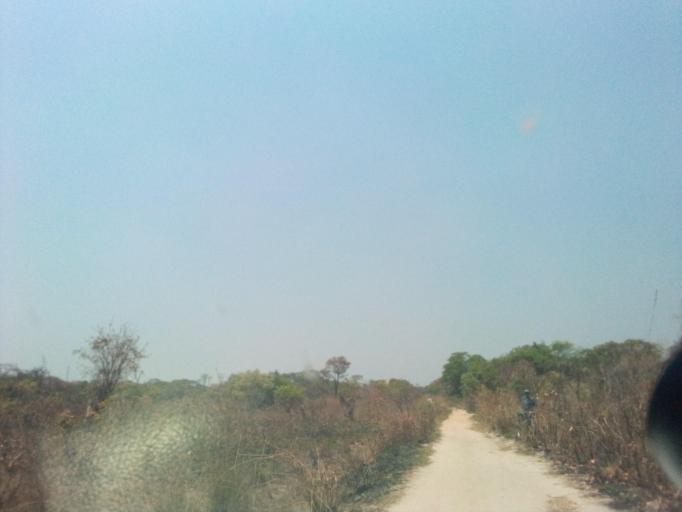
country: ZM
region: Copperbelt
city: Kataba
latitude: -12.2448
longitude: 30.3297
